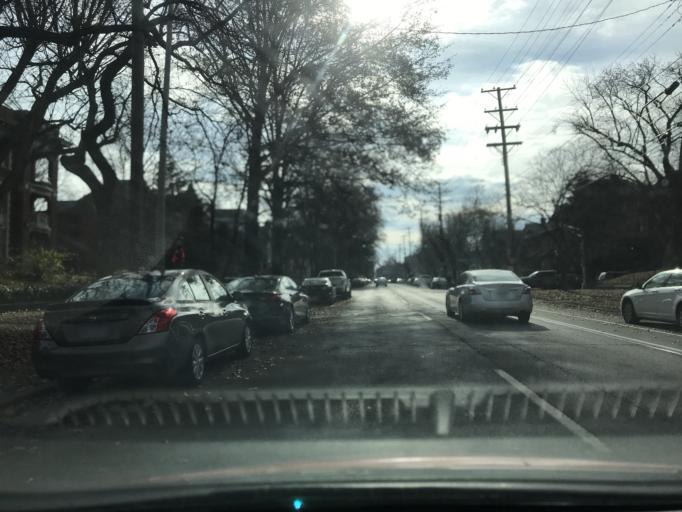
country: US
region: Kentucky
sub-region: Jefferson County
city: Louisville
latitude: 38.2237
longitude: -85.7606
